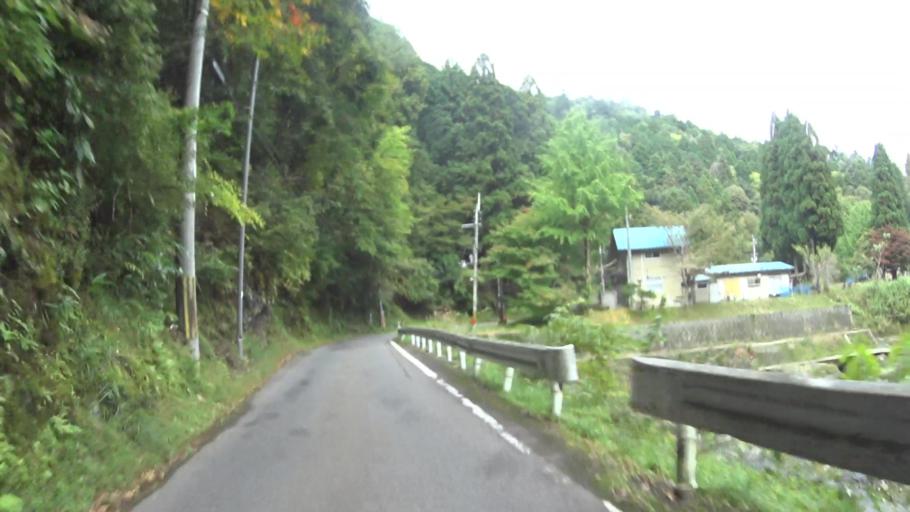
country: JP
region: Shiga Prefecture
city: Kitahama
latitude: 35.2098
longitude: 135.7746
